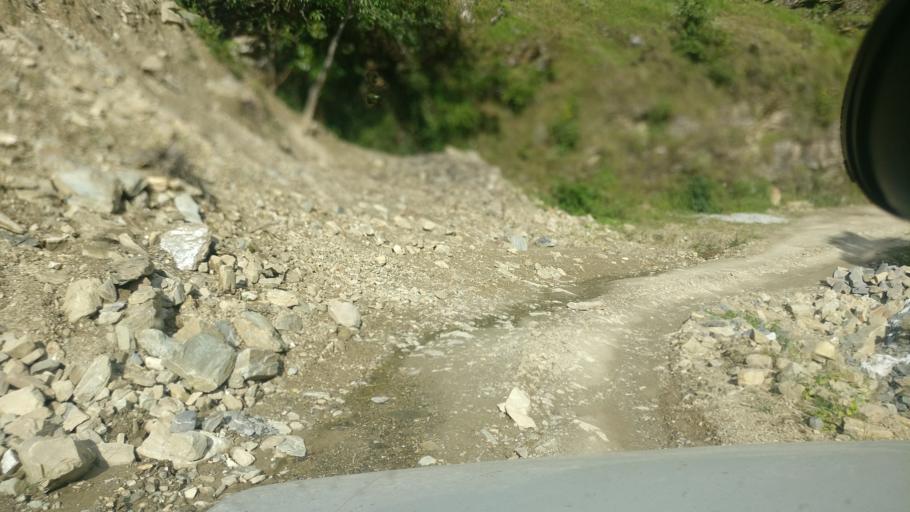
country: NP
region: Western Region
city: Baglung
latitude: 28.2721
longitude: 83.6477
